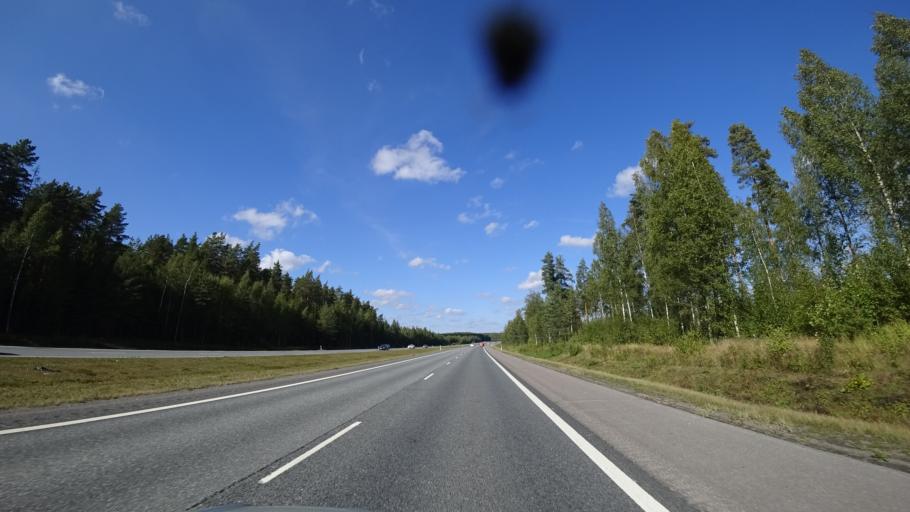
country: FI
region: Haeme
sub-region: Haemeenlinna
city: Janakkala
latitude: 60.9264
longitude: 24.5231
